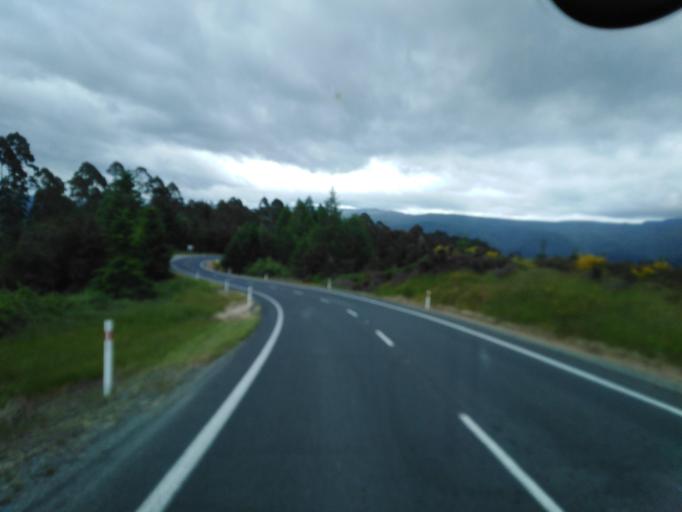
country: NZ
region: Tasman
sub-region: Tasman District
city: Wakefield
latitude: -41.6292
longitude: 172.7081
